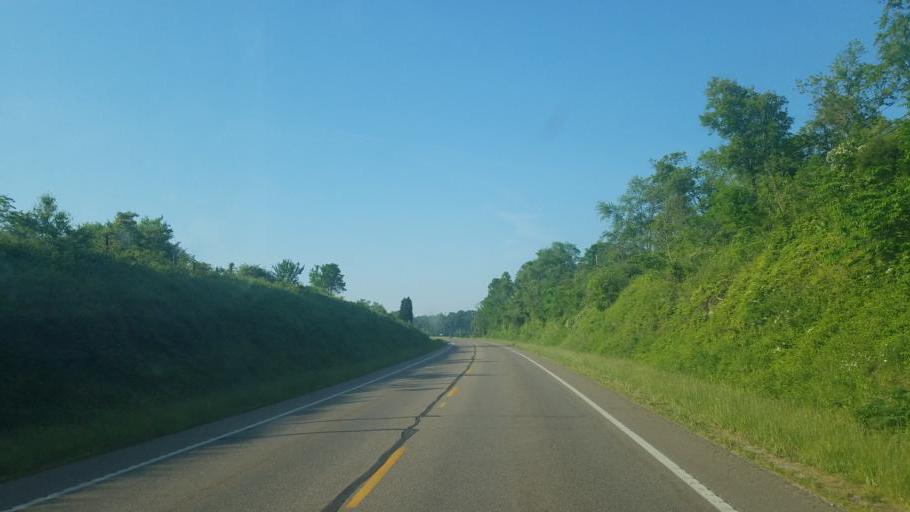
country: US
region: West Virginia
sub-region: Mason County
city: New Haven
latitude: 39.0968
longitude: -81.9269
